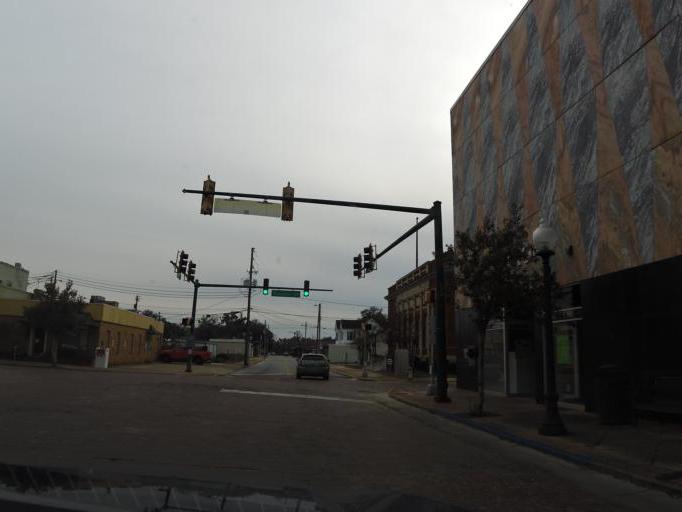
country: US
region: Georgia
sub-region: Decatur County
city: Bainbridge
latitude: 30.9061
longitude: -84.5765
